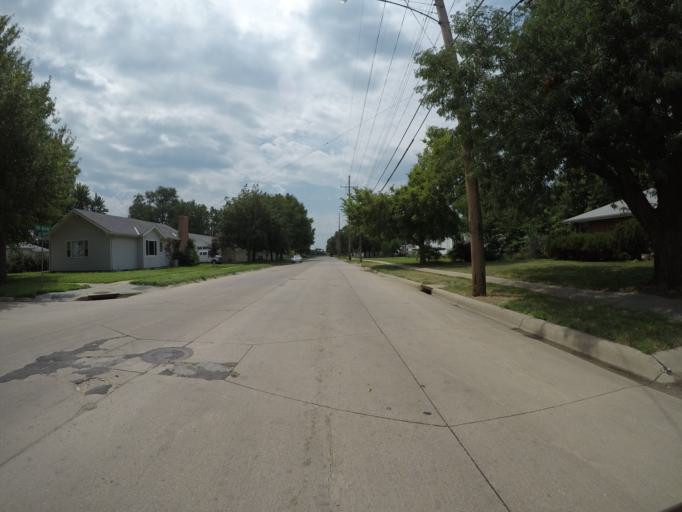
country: US
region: Nebraska
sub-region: Buffalo County
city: Kearney
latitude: 40.6969
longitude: -99.1014
